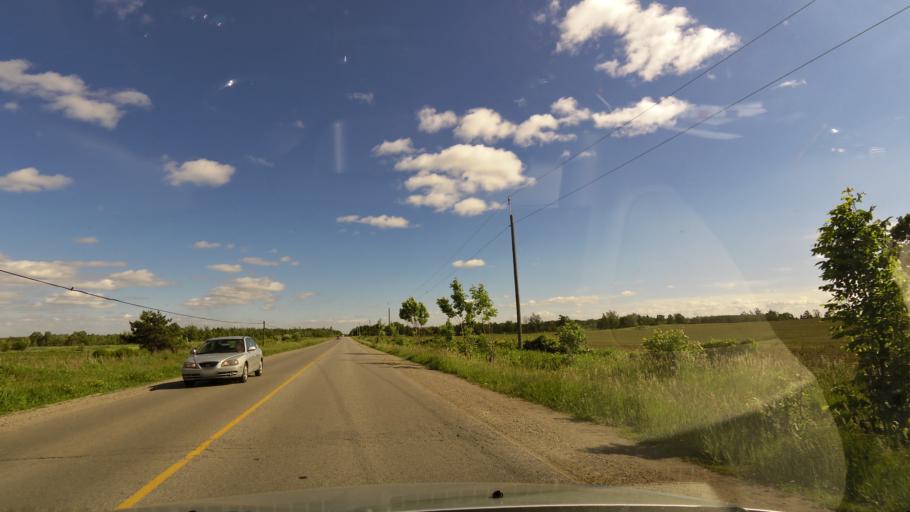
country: CA
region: Ontario
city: Bradford West Gwillimbury
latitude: 44.1590
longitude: -79.6153
